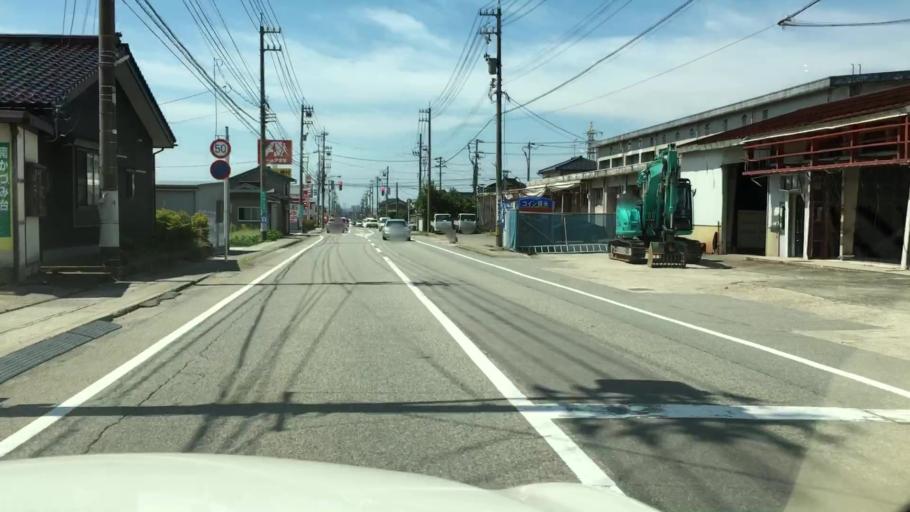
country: JP
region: Toyama
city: Kamiichi
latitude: 36.6996
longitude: 137.3586
